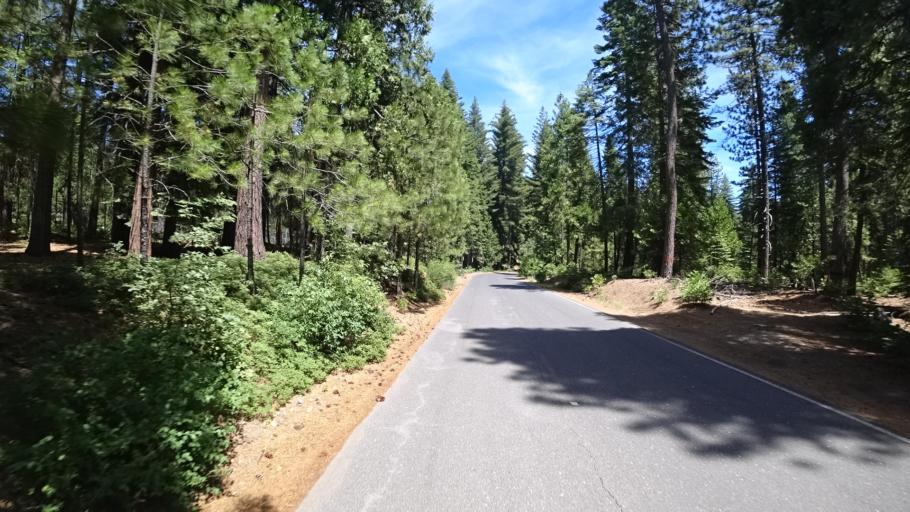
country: US
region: California
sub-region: Calaveras County
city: Arnold
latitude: 38.2976
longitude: -120.2628
